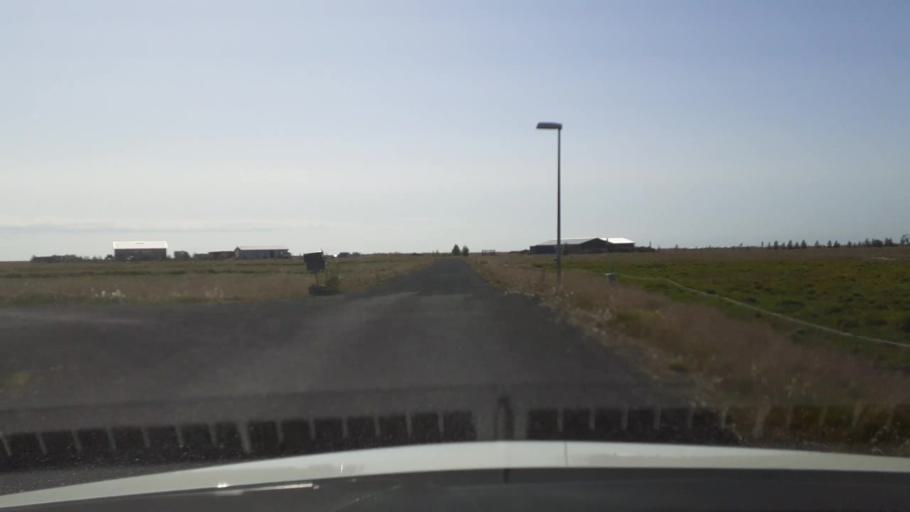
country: IS
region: South
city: Selfoss
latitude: 63.8875
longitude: -21.0910
